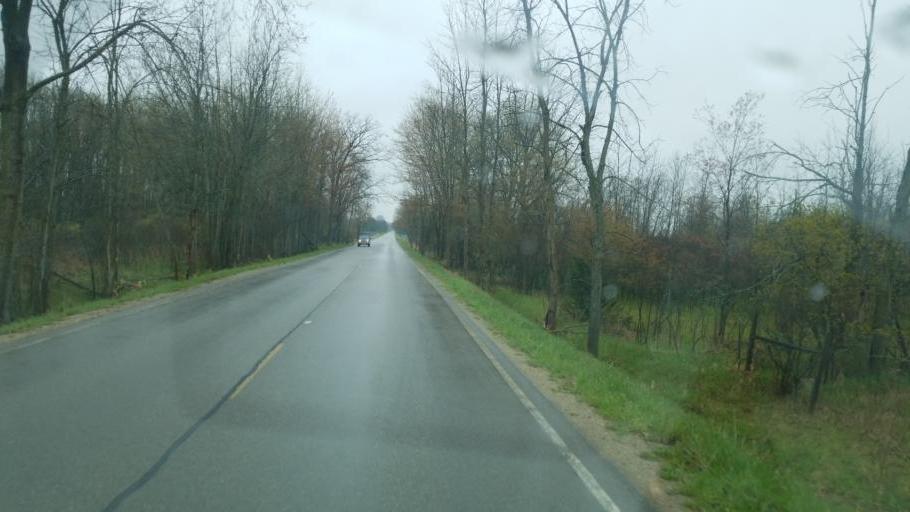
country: US
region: Michigan
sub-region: Montcalm County
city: Lakeview
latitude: 43.4894
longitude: -85.3045
